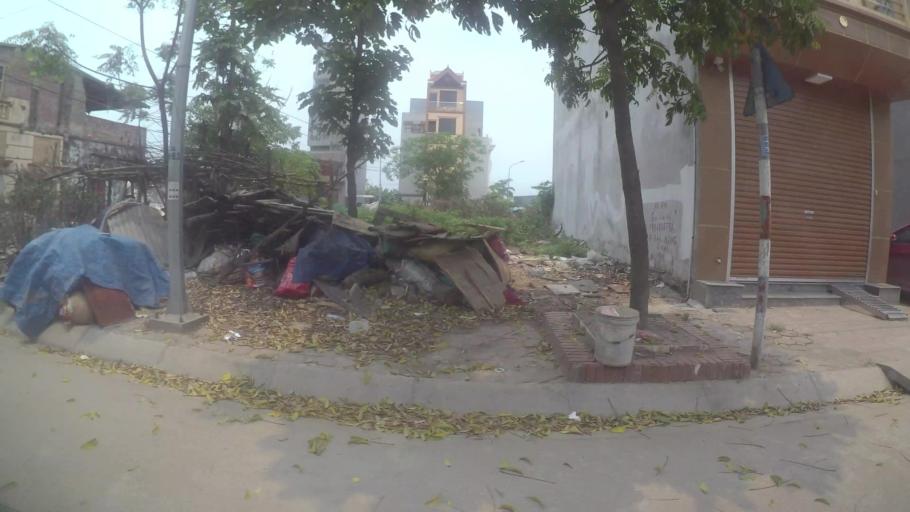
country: VN
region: Ha Noi
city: Ha Dong
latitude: 20.9906
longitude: 105.7419
